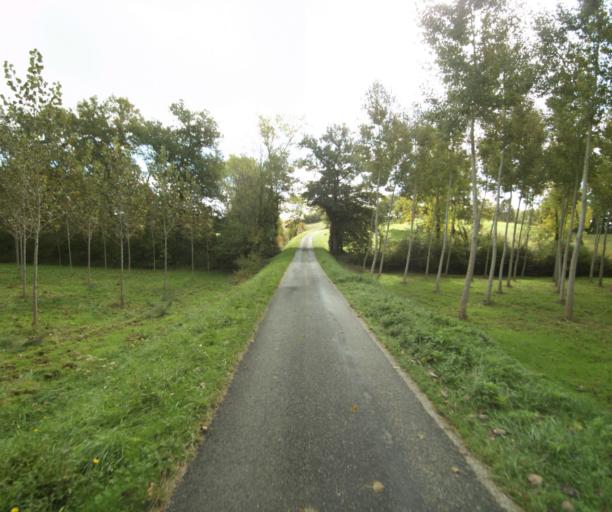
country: FR
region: Midi-Pyrenees
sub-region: Departement du Gers
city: Nogaro
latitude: 43.8346
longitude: -0.0764
